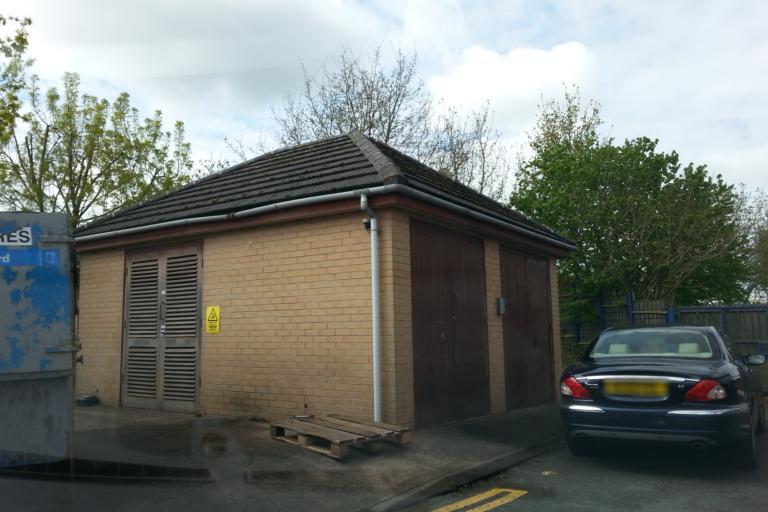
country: GB
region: England
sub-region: Staffordshire
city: Shenstone
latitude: 52.6517
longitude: -1.8361
